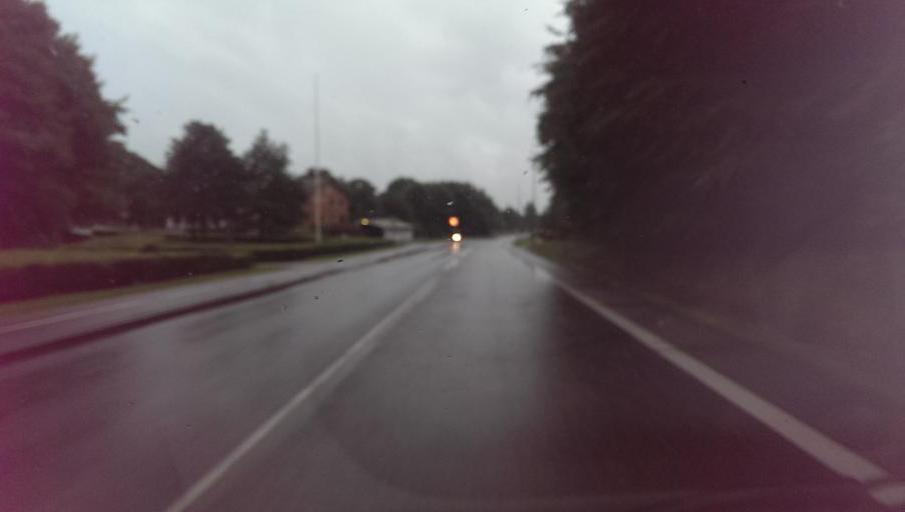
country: DK
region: South Denmark
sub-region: Vejle Kommune
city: Give
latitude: 55.8502
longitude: 9.2402
